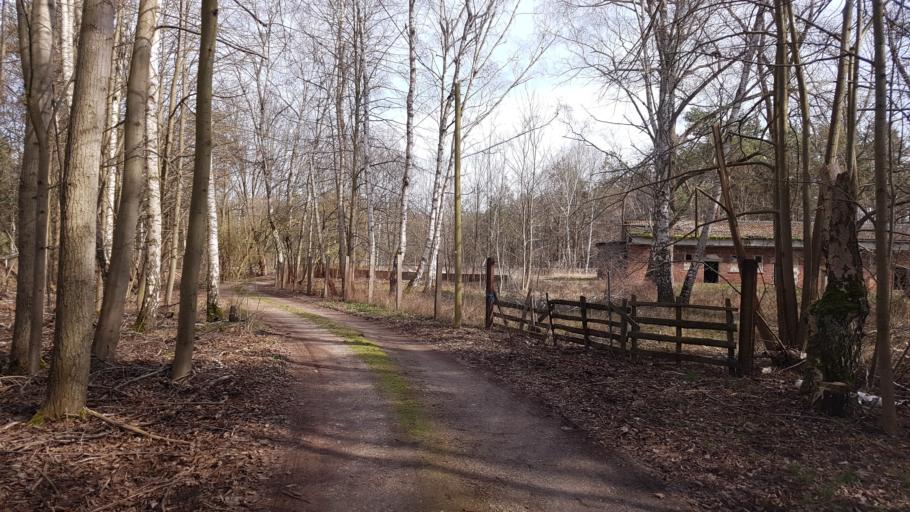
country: DE
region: Brandenburg
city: Doberlug-Kirchhain
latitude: 51.6264
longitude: 13.6161
